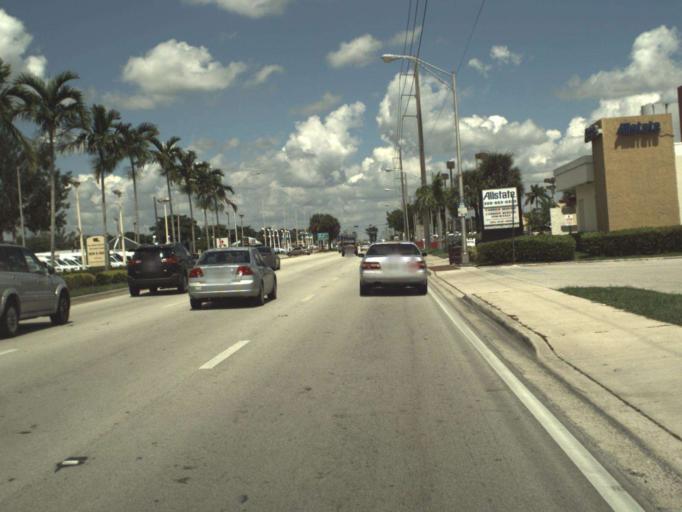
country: US
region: Florida
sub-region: Miami-Dade County
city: Andover
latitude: 25.9678
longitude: -80.2059
